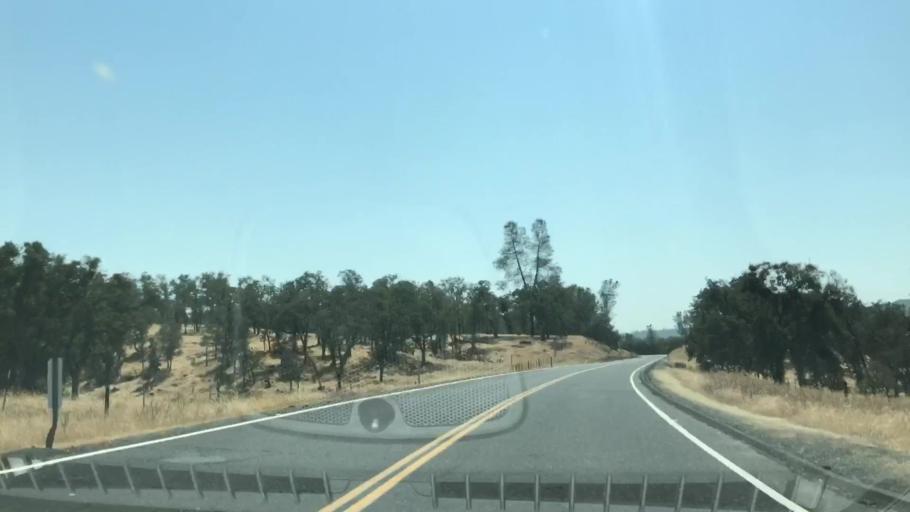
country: US
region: California
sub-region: Calaveras County
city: Copperopolis
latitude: 37.9565
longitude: -120.6133
